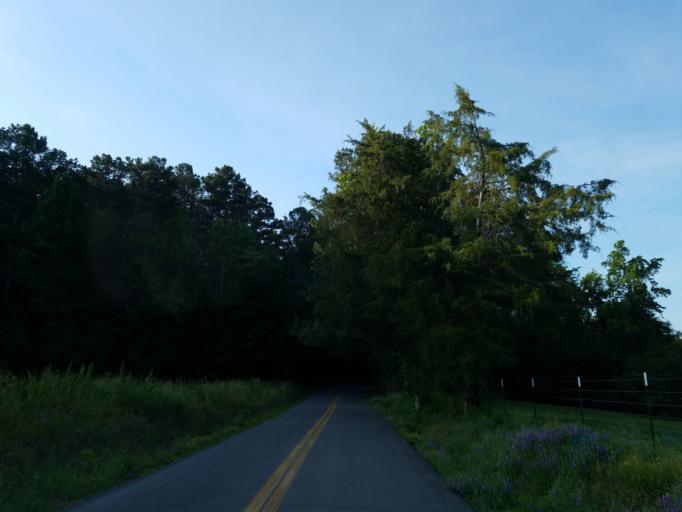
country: US
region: Georgia
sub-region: Gordon County
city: Calhoun
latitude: 34.5242
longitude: -85.1197
